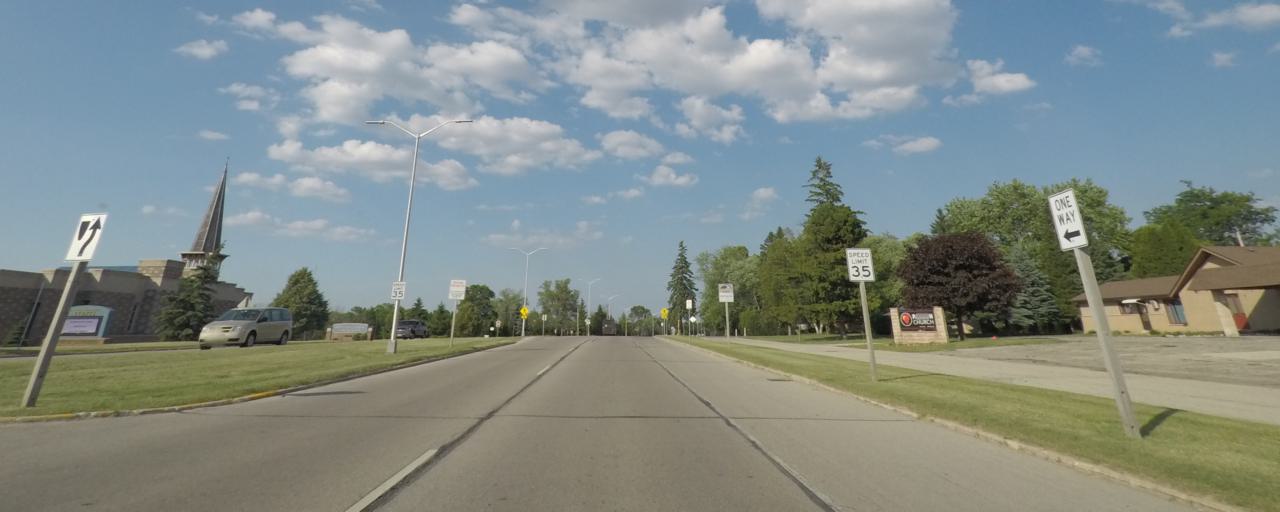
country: US
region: Wisconsin
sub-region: Milwaukee County
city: Hales Corners
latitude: 42.9335
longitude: -88.0690
